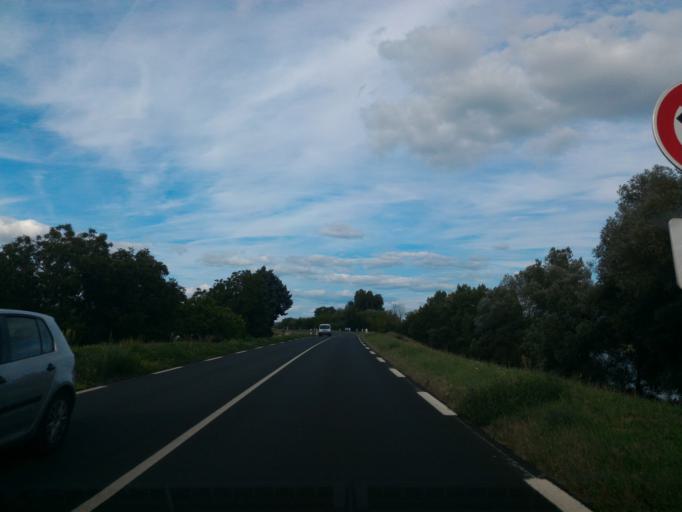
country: FR
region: Centre
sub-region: Departement du Loir-et-Cher
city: Chouzy-sur-Cisse
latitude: 47.5316
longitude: 1.2672
